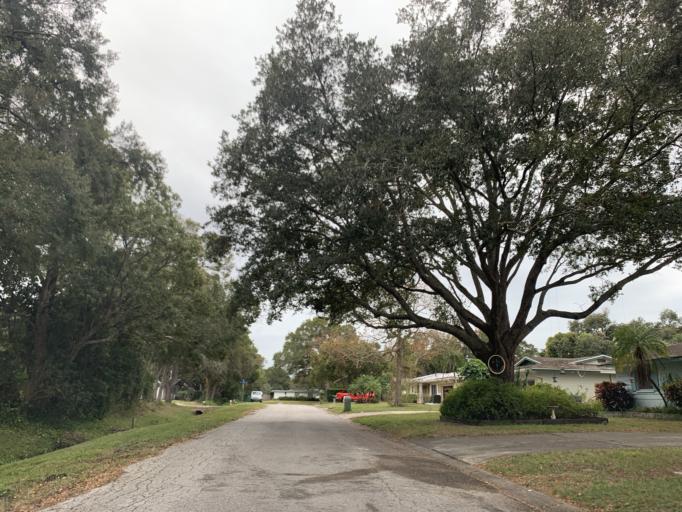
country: US
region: Florida
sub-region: Pinellas County
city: Belleair
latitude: 27.9364
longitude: -82.7793
